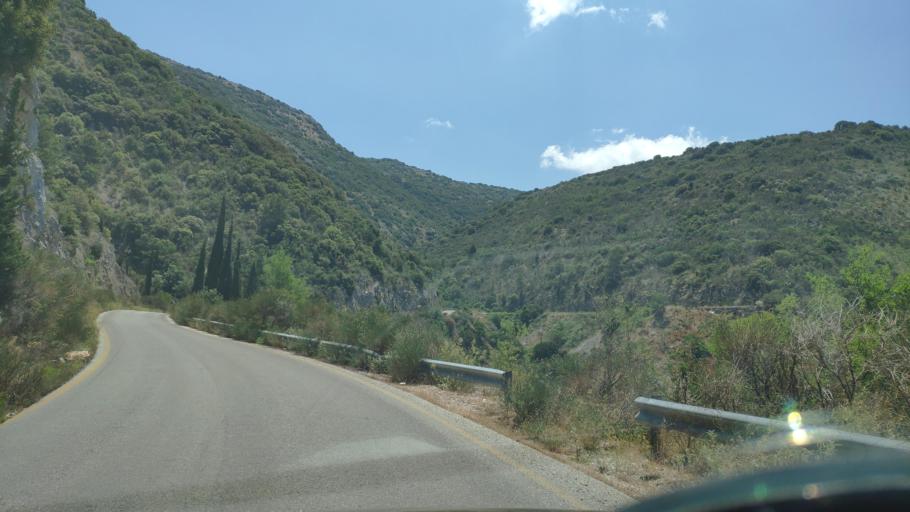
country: GR
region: Ionian Islands
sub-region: Lefkada
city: Nidri
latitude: 38.7468
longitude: 20.6203
